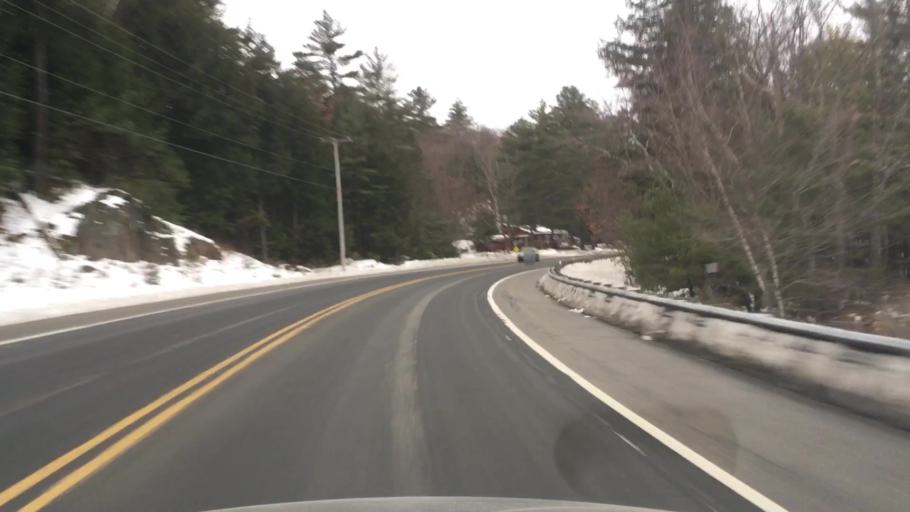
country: US
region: New Hampshire
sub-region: Merrimack County
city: Henniker
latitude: 43.2175
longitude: -71.8785
